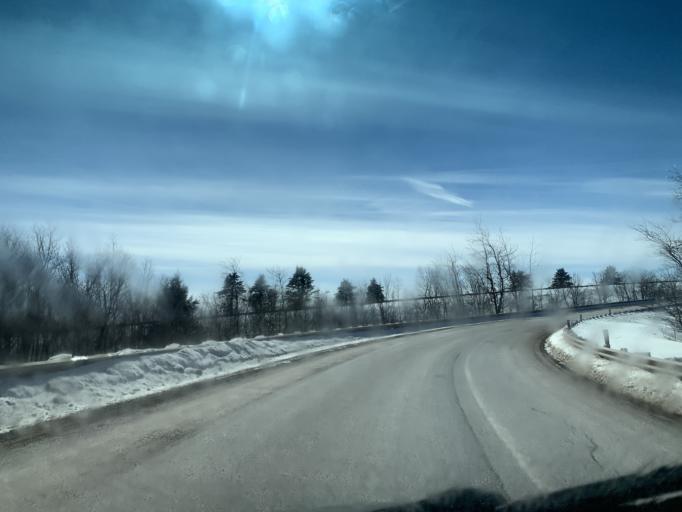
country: US
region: Pennsylvania
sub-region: Somerset County
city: Meyersdale
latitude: 39.6873
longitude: -79.2479
